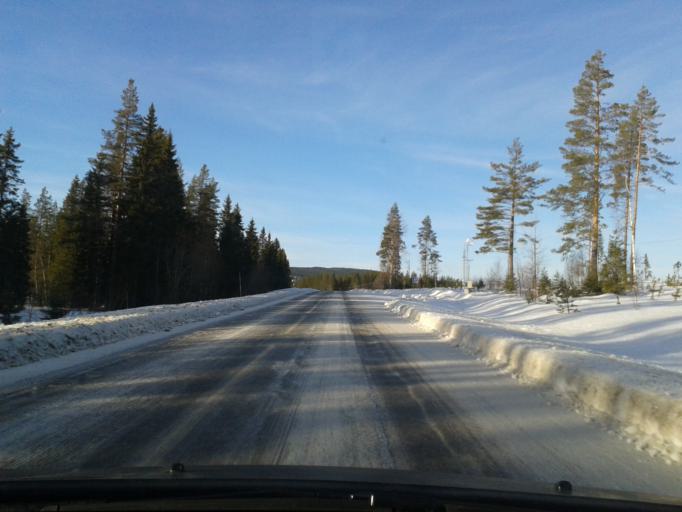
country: SE
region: Vaesterbotten
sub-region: Asele Kommun
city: Asele
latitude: 63.7695
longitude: 17.6817
